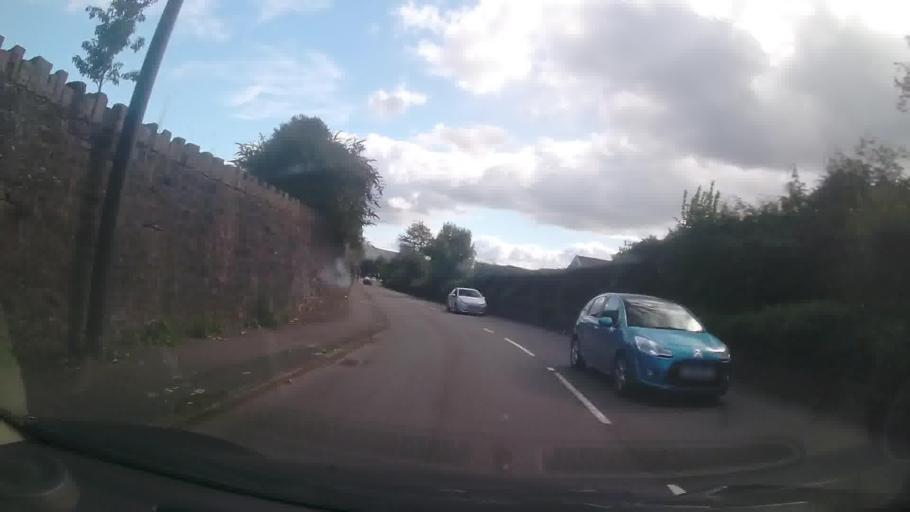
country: GB
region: Wales
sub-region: Merthyr Tydfil County Borough
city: Merthyr Tydfil
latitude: 51.7561
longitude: -3.3939
